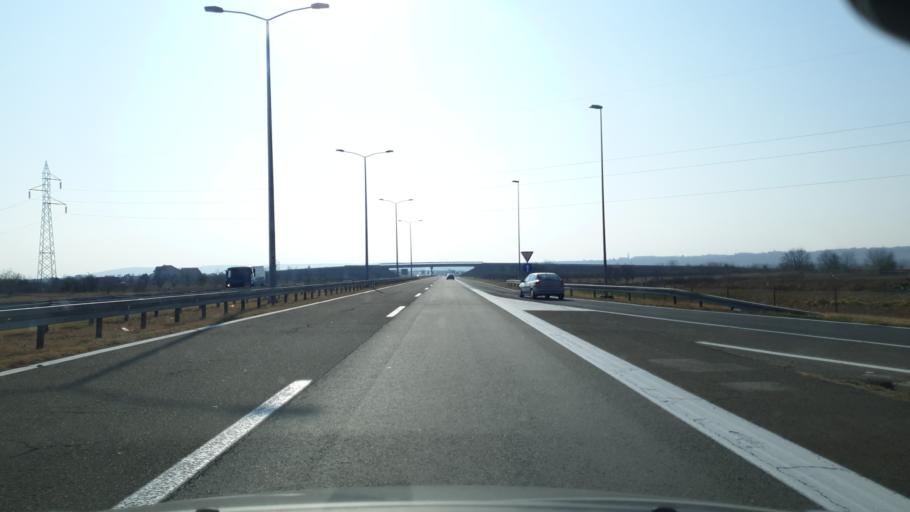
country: RS
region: Central Serbia
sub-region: Nisavski Okrug
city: Nis
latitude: 43.3250
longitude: 21.8089
